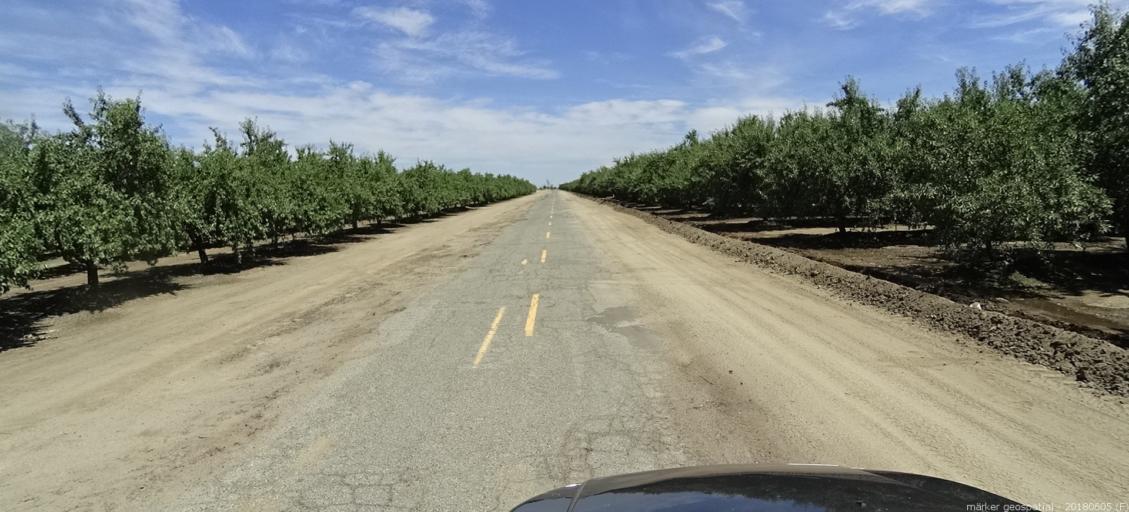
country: US
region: California
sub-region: Madera County
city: Chowchilla
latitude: 37.0589
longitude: -120.4192
